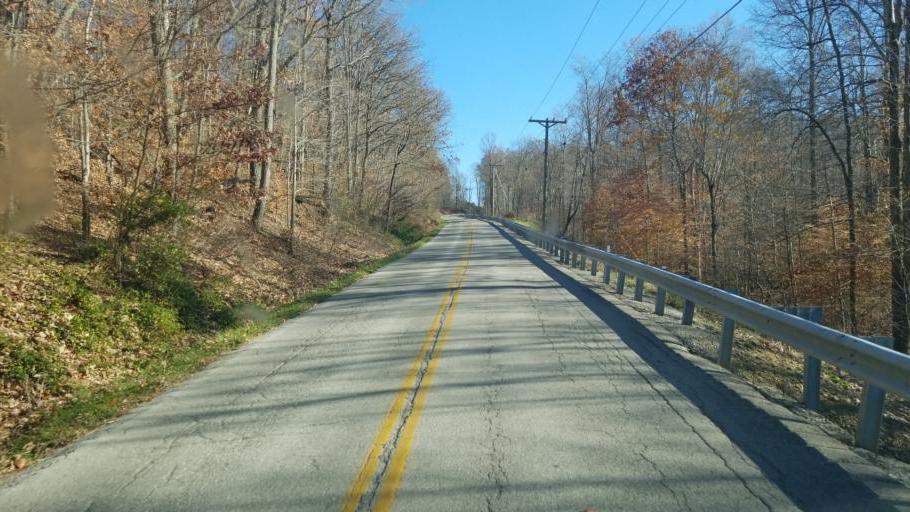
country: US
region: Kentucky
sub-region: Fleming County
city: Flemingsburg
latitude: 38.4637
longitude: -83.5330
